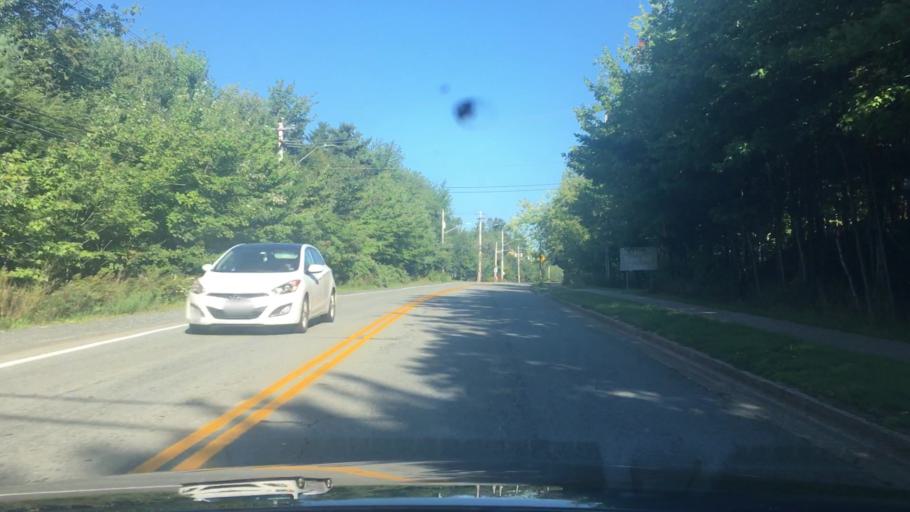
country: CA
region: Nova Scotia
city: Dartmouth
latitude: 44.7176
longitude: -63.6839
